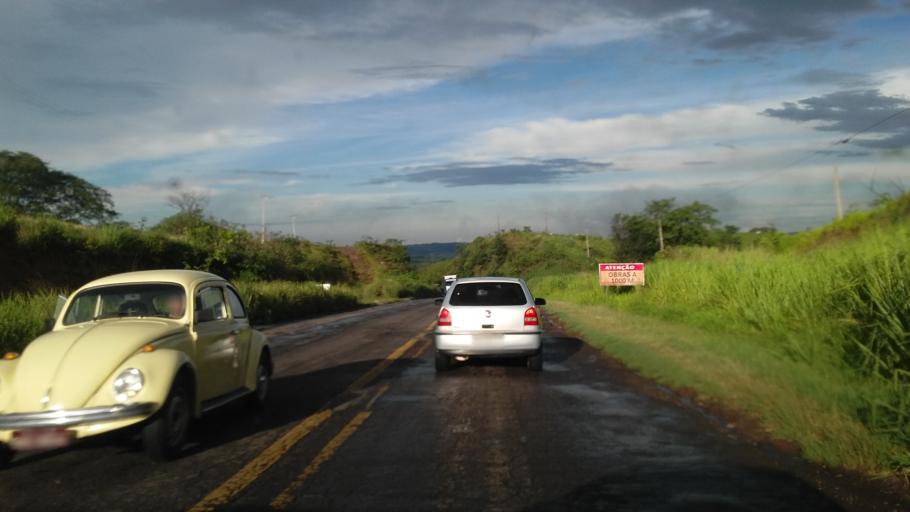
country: BR
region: Sao Paulo
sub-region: Marilia
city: Marilia
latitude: -22.1273
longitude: -49.9363
